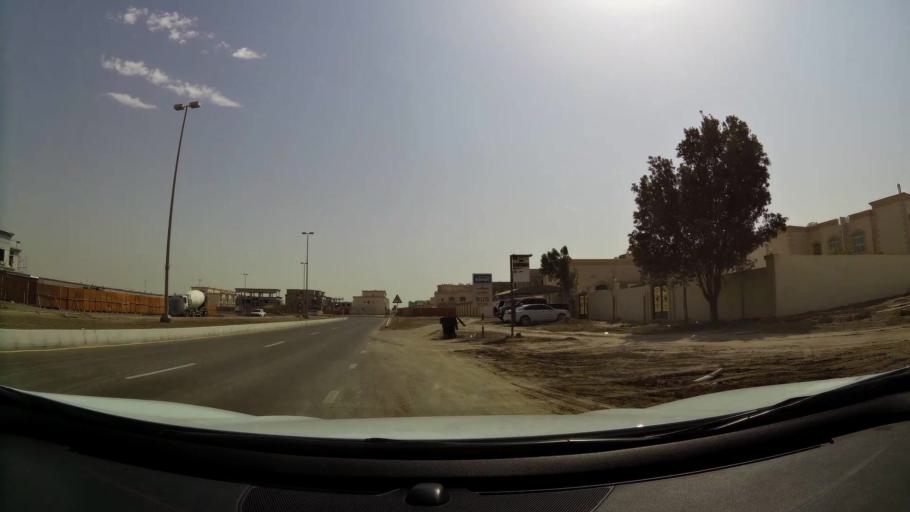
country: AE
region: Abu Dhabi
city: Abu Dhabi
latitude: 24.3338
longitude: 54.5487
